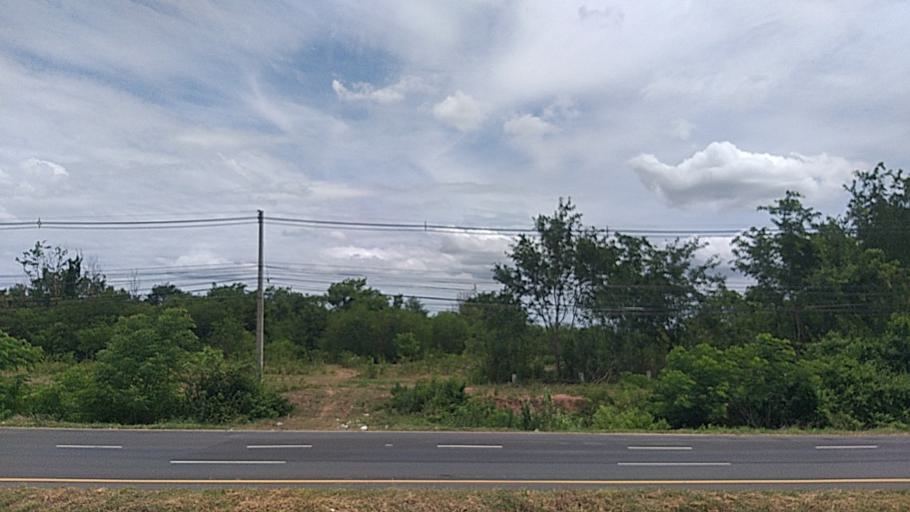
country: TH
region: Buriram
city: Prakhon Chai
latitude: 14.6078
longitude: 103.1084
